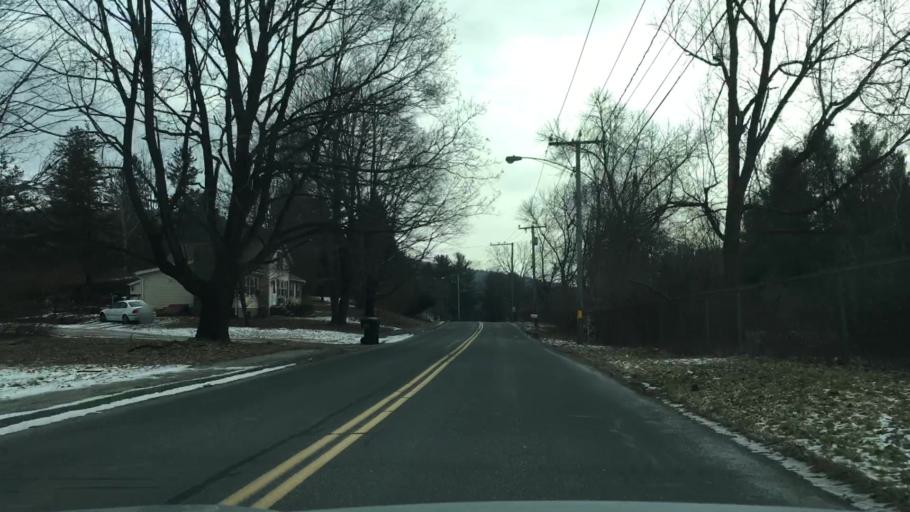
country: US
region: Massachusetts
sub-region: Berkshire County
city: Lee
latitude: 42.2945
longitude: -73.2469
